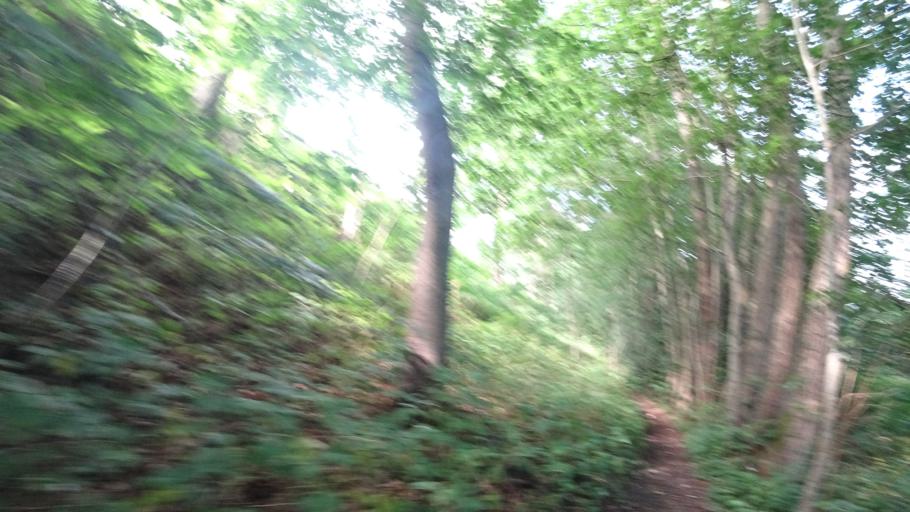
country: DE
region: North Rhine-Westphalia
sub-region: Regierungsbezirk Detmold
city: Steinhagen
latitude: 51.9436
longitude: 8.4448
